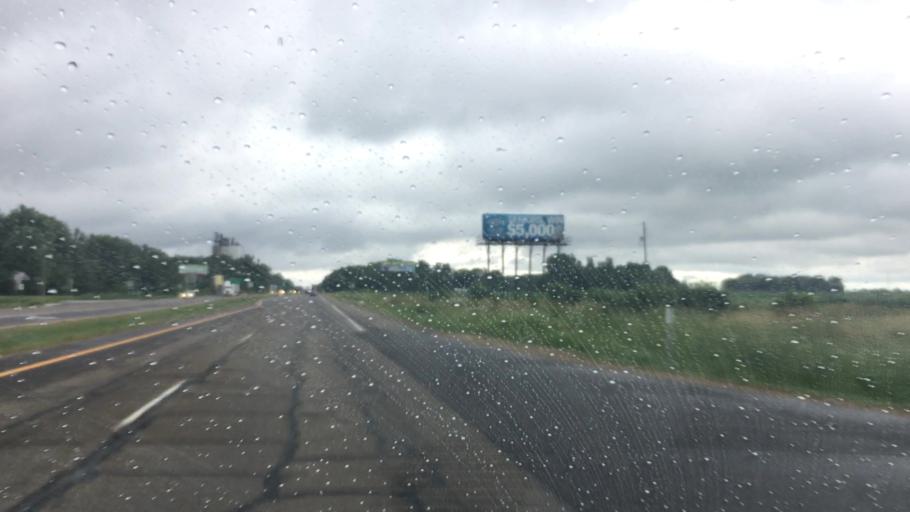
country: US
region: Michigan
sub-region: Ottawa County
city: Beechwood
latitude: 42.8626
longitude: -86.1084
